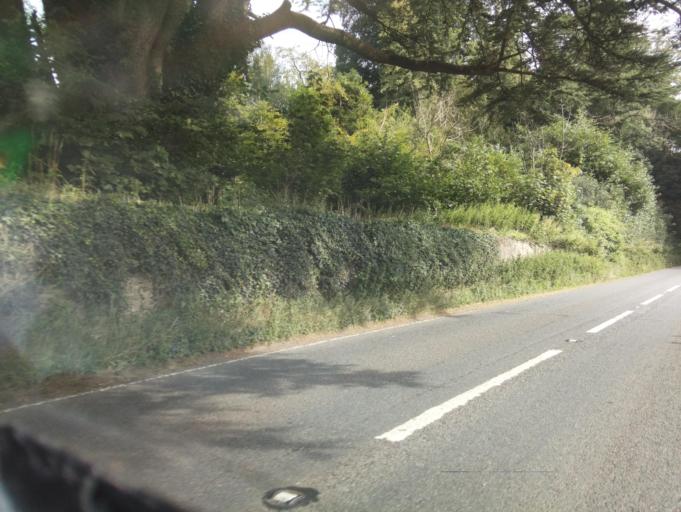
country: GB
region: England
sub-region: Bath and North East Somerset
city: East Harptree
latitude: 51.2703
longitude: -2.5856
